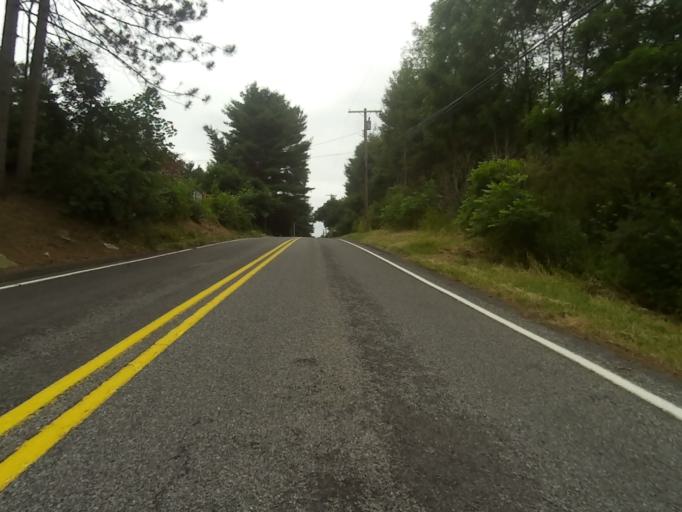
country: US
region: Pennsylvania
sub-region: Centre County
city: Stormstown
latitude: 40.7165
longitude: -78.0017
